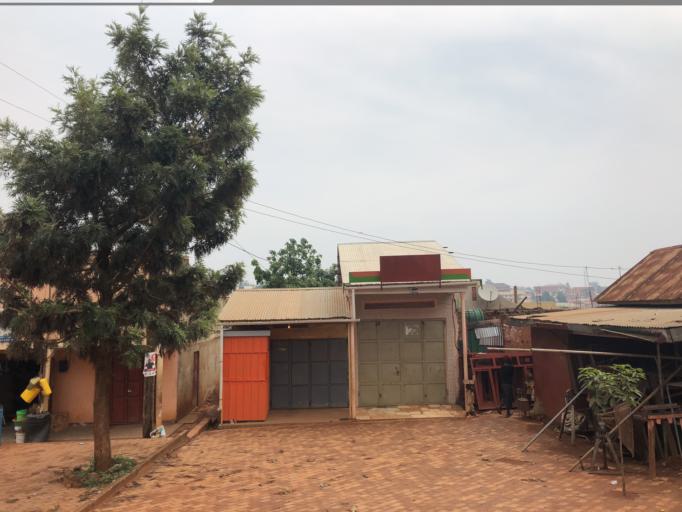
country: UG
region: Central Region
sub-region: Mukono District
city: Mukono
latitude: 0.3573
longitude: 32.7498
